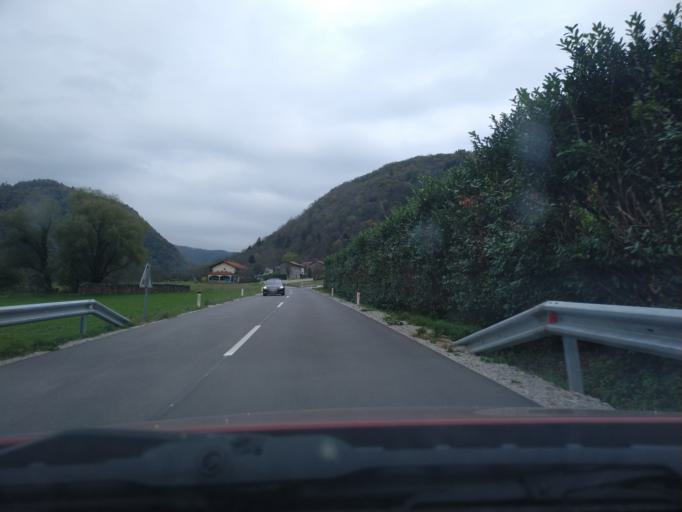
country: SI
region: Tolmin
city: Tolmin
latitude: 46.1660
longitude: 13.7096
